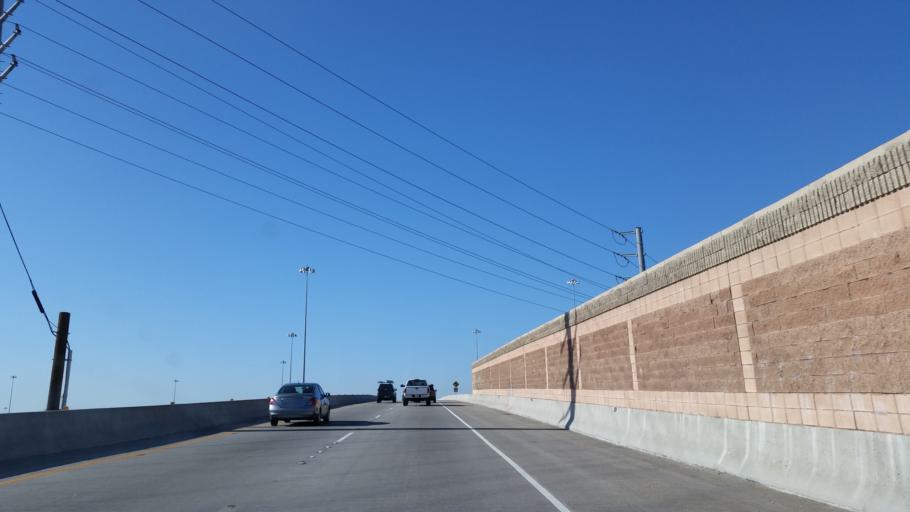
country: US
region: California
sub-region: Orange County
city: Buena Park
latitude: 33.8555
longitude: -117.9757
